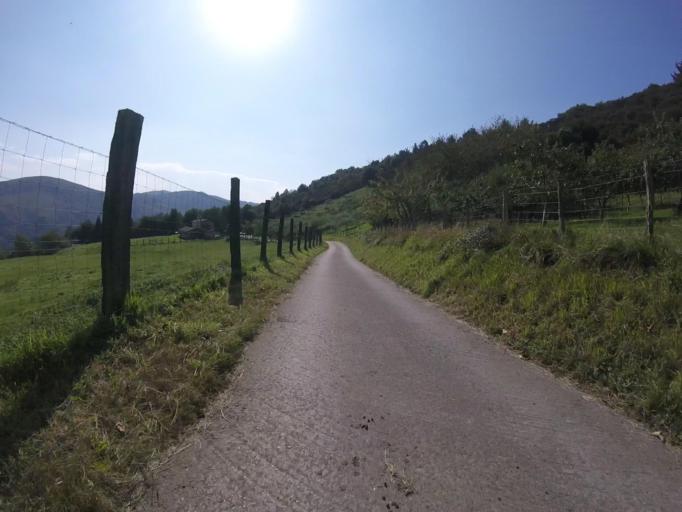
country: ES
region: Basque Country
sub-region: Provincia de Guipuzcoa
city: Irun
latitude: 43.3276
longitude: -1.7586
